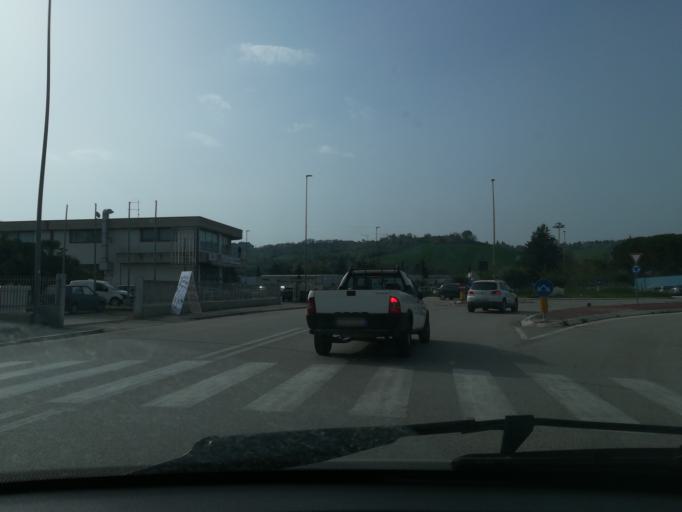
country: IT
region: The Marches
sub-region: Provincia di Macerata
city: Piediripa
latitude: 43.2808
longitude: 13.4890
